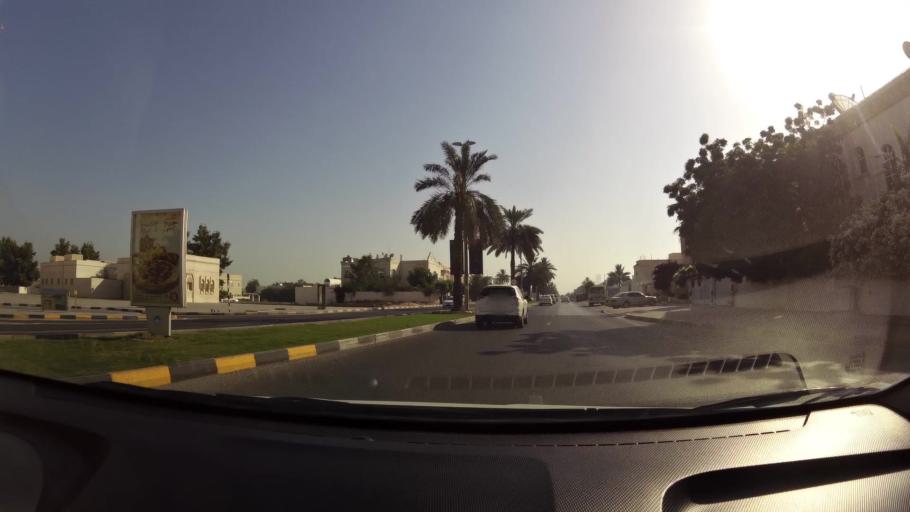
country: AE
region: Ash Shariqah
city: Sharjah
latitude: 25.3771
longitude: 55.4025
